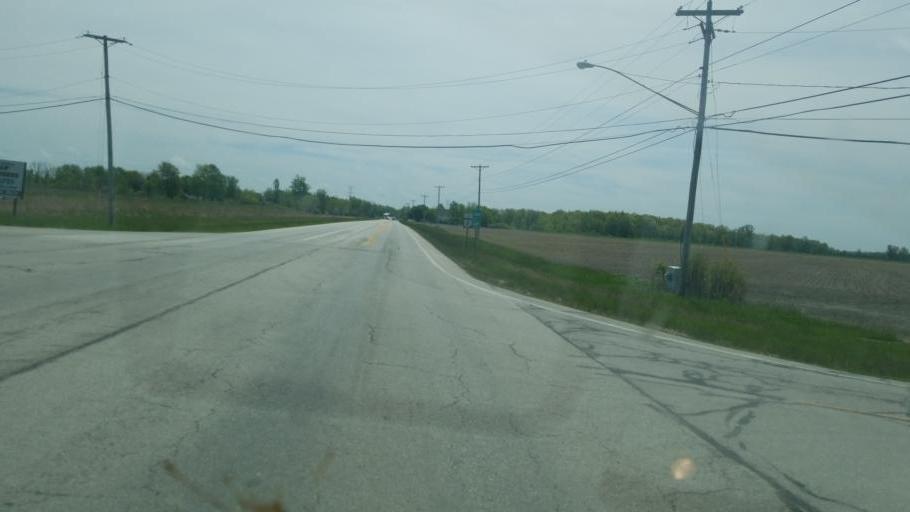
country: US
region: Ohio
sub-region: Ottawa County
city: Oak Harbor
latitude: 41.5666
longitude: -83.0801
